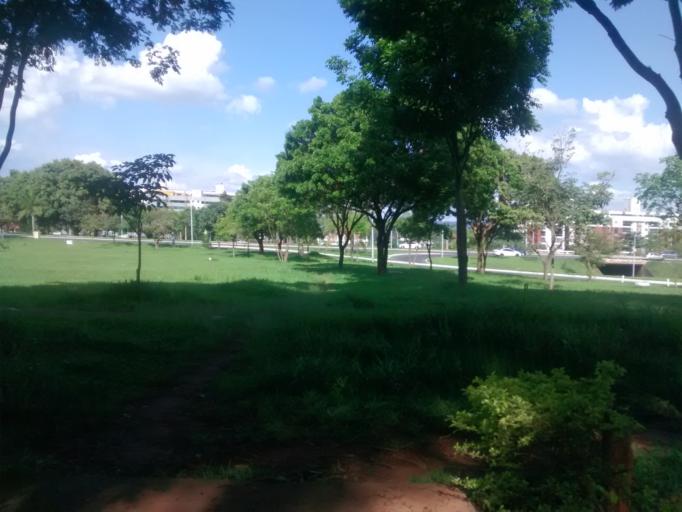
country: BR
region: Federal District
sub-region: Brasilia
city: Brasilia
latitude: -15.7458
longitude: -47.8912
